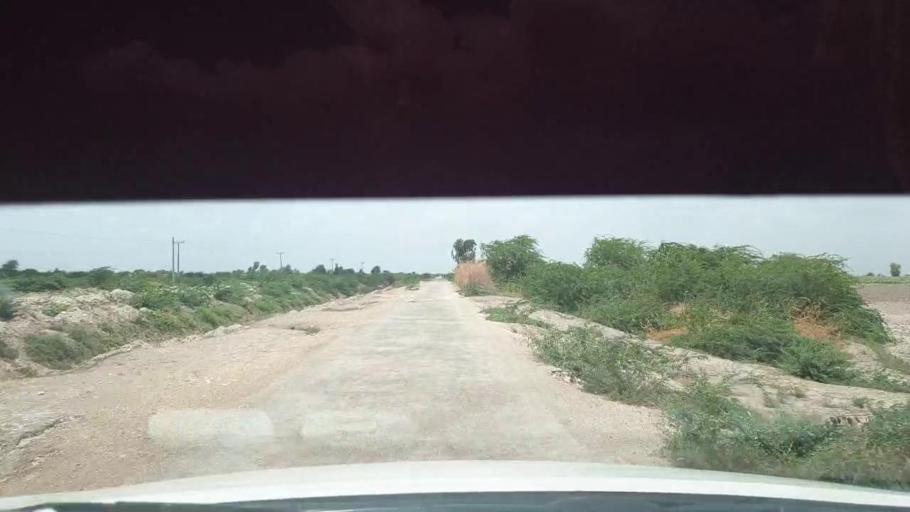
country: PK
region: Sindh
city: Kadhan
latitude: 24.5350
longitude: 69.1262
